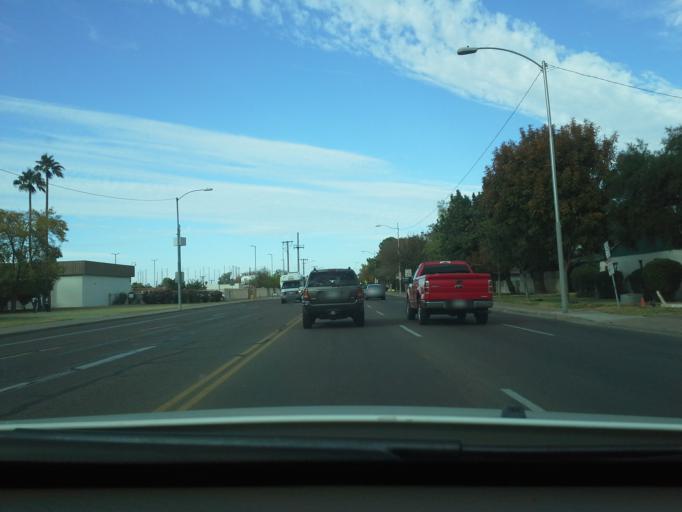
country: US
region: Arizona
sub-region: Maricopa County
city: Phoenix
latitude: 33.4810
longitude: -112.1000
